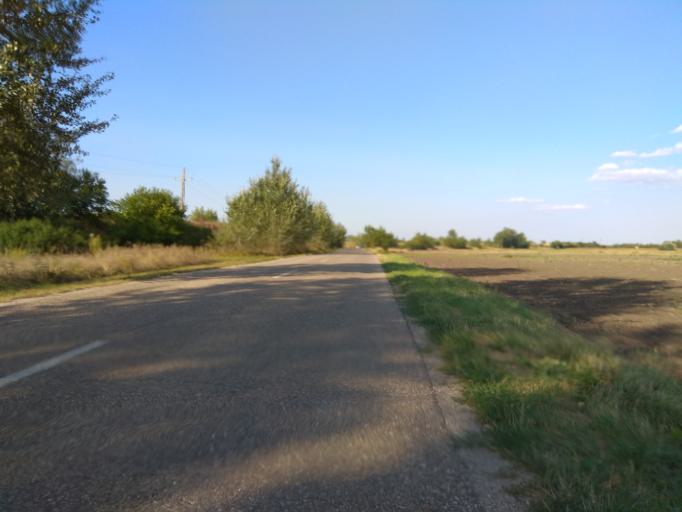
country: HU
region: Borsod-Abauj-Zemplen
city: Onod
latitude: 47.9688
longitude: 20.8851
